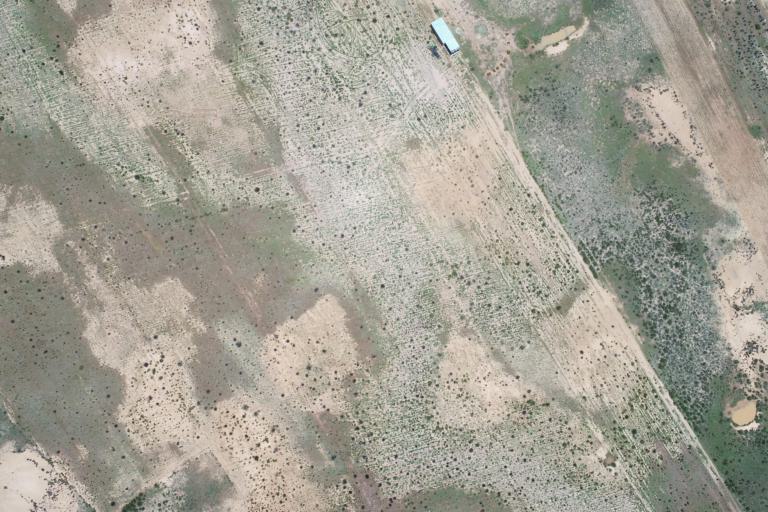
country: BO
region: La Paz
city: Patacamaya
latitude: -17.2848
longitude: -68.5031
